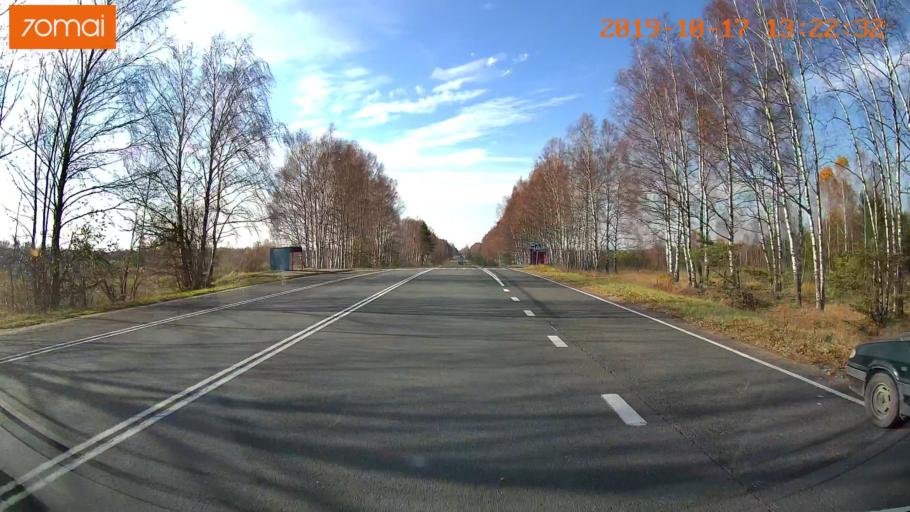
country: RU
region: Rjazan
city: Gus'-Zheleznyy
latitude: 55.0863
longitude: 41.0006
